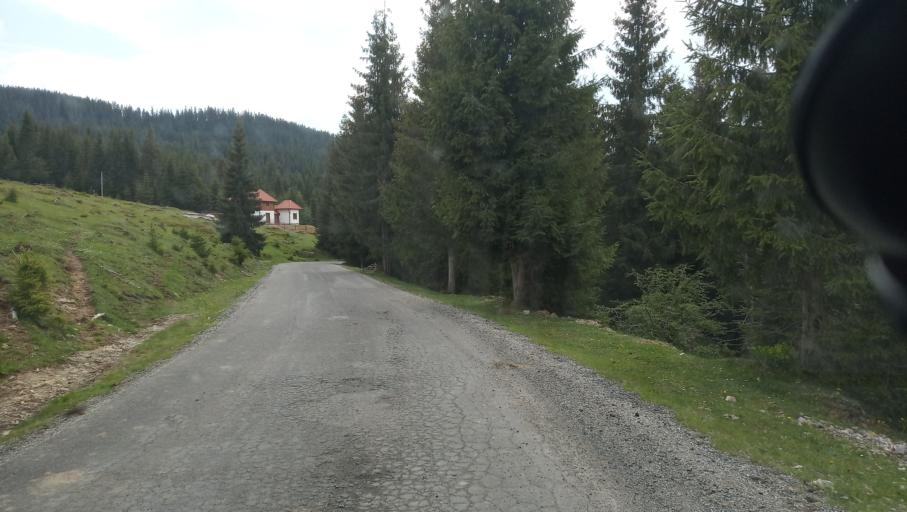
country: RO
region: Alba
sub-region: Comuna Horea
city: Horea
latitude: 46.5487
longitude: 22.8975
